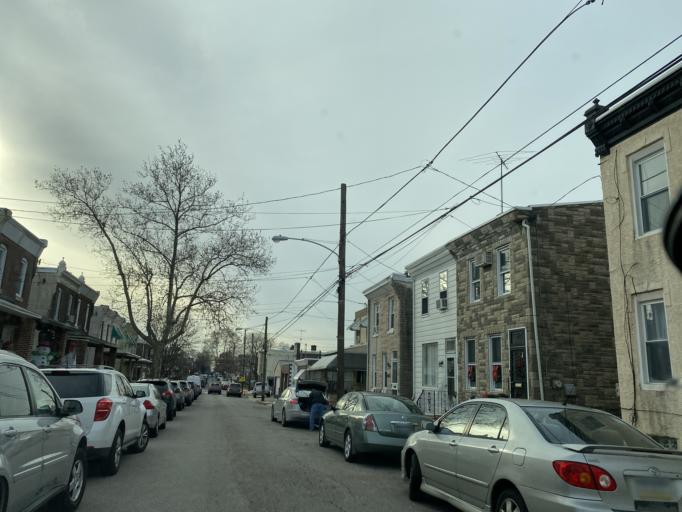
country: US
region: New Jersey
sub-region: Burlington County
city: Palmyra
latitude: 40.0278
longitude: -75.0370
